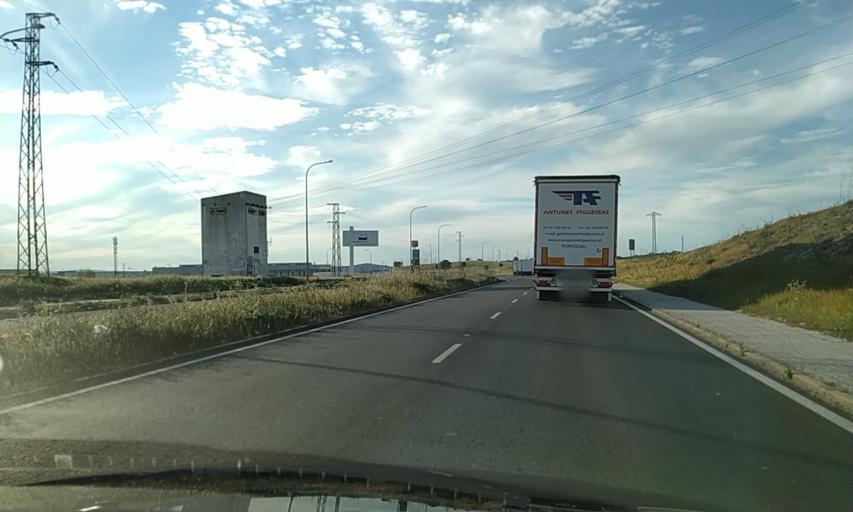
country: ES
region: Extremadura
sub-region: Provincia de Badajoz
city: Badajoz
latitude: 38.8990
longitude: -6.9869
